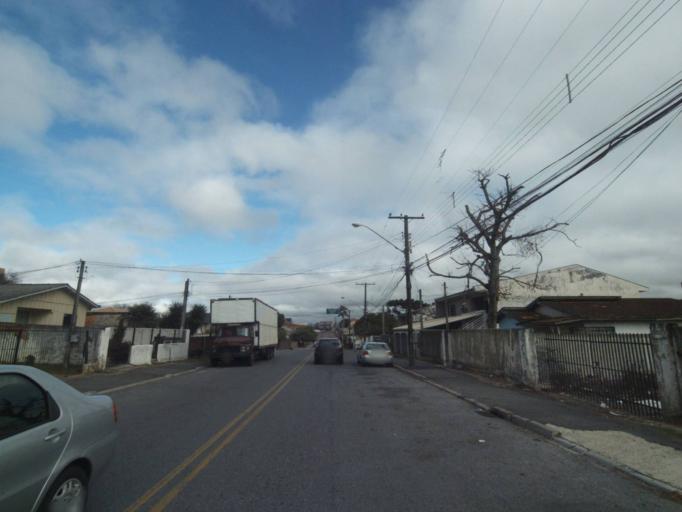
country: BR
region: Parana
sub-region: Sao Jose Dos Pinhais
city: Sao Jose dos Pinhais
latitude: -25.5203
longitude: -49.2977
